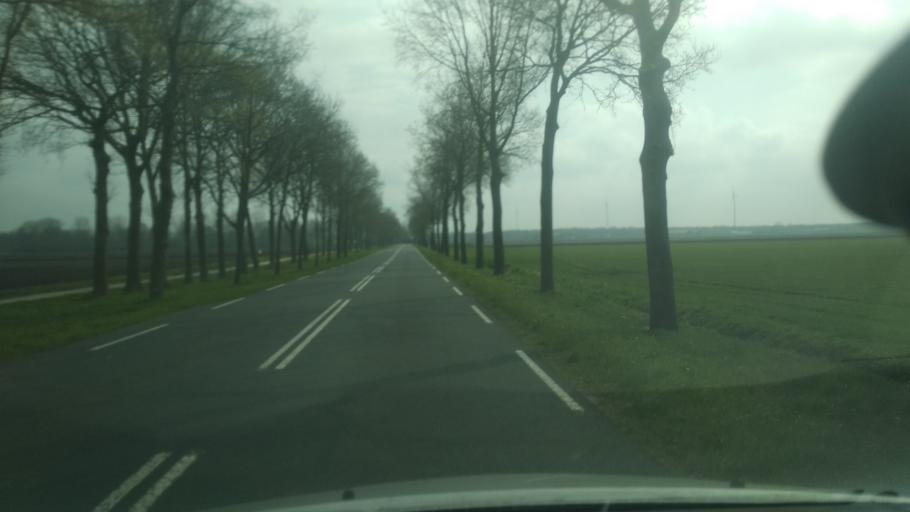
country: NL
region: Groningen
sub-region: Gemeente Stadskanaal
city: Stadskanaal
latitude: 52.8978
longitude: 6.9000
